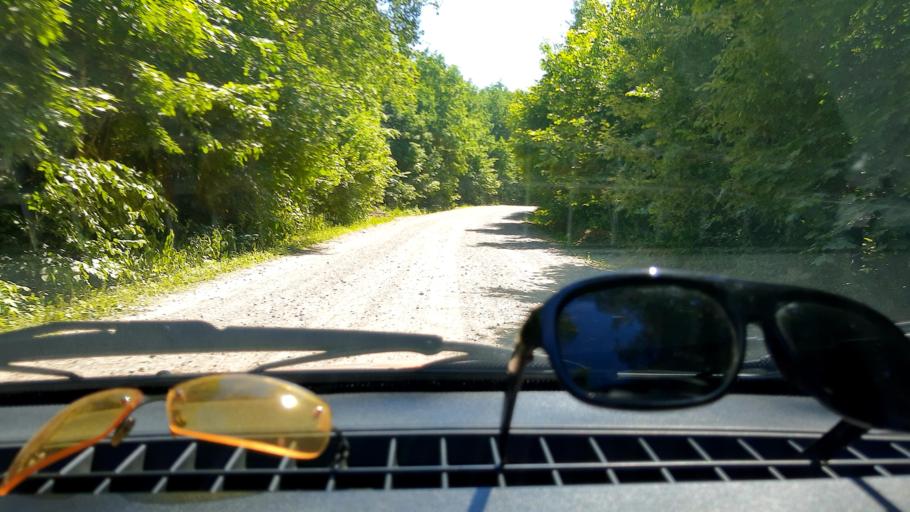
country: RU
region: Bashkortostan
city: Ulu-Telyak
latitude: 54.7991
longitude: 57.0267
